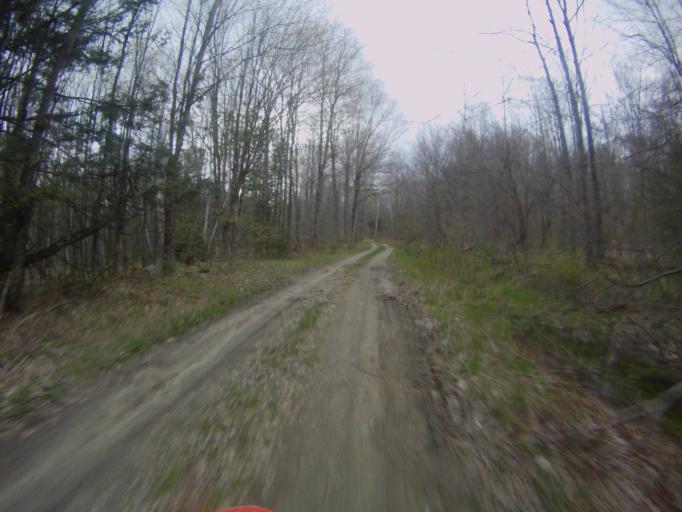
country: US
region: Vermont
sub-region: Addison County
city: Bristol
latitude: 44.0545
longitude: -73.0504
